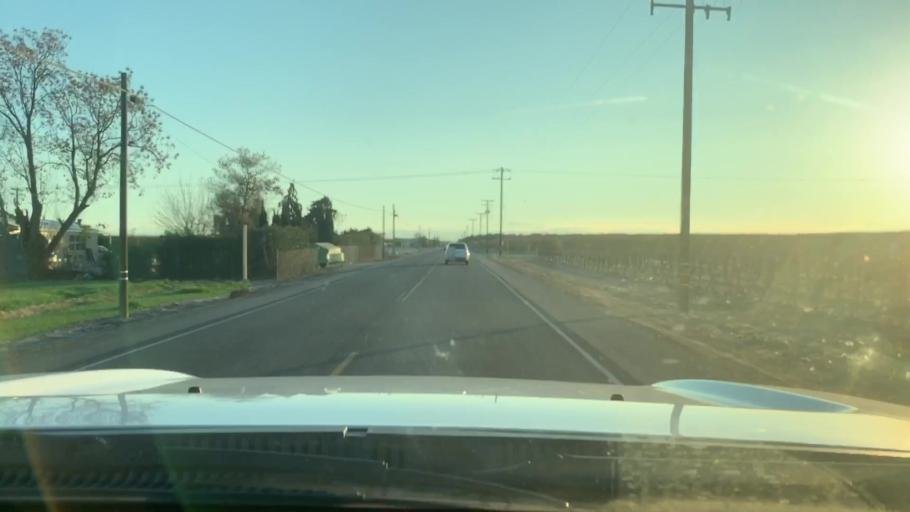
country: US
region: California
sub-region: Kern County
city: Shafter
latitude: 35.4995
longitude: -119.3150
